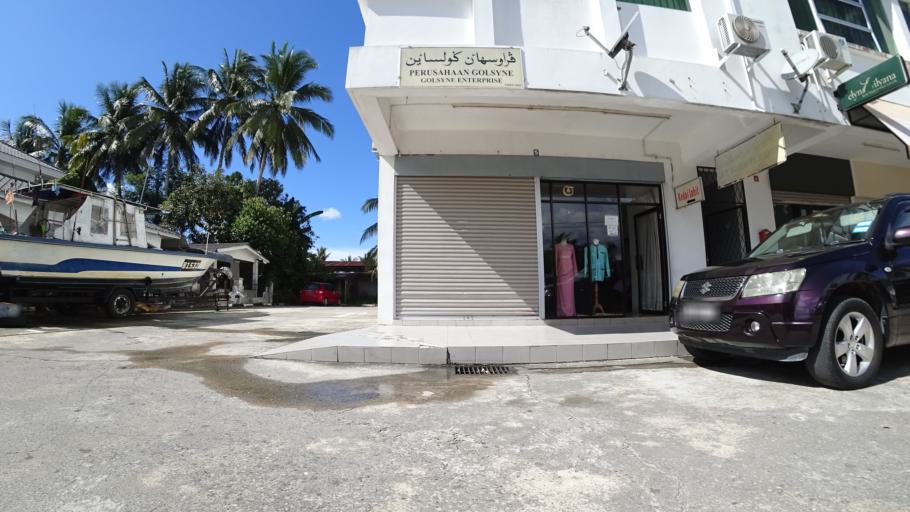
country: BN
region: Brunei and Muara
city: Bandar Seri Begawan
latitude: 4.8779
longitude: 114.8449
